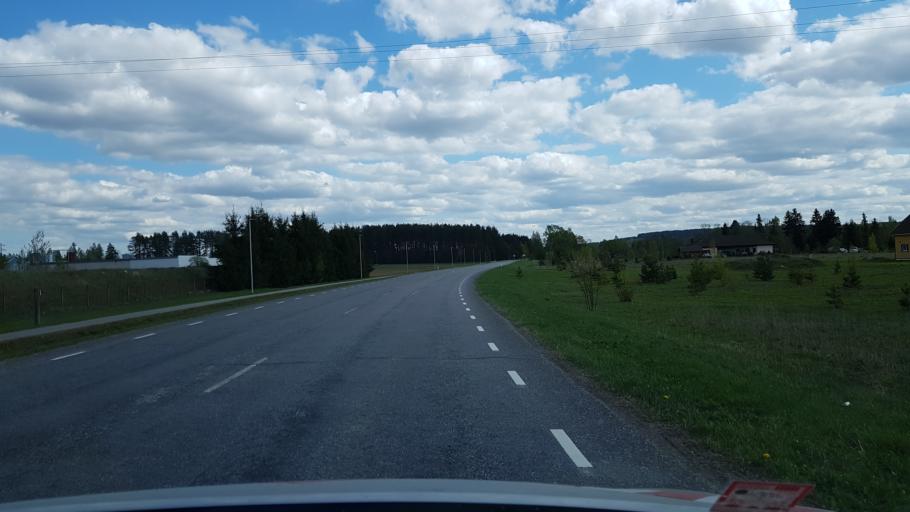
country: EE
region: Tartu
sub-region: UElenurme vald
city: Ulenurme
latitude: 58.3058
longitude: 26.8574
